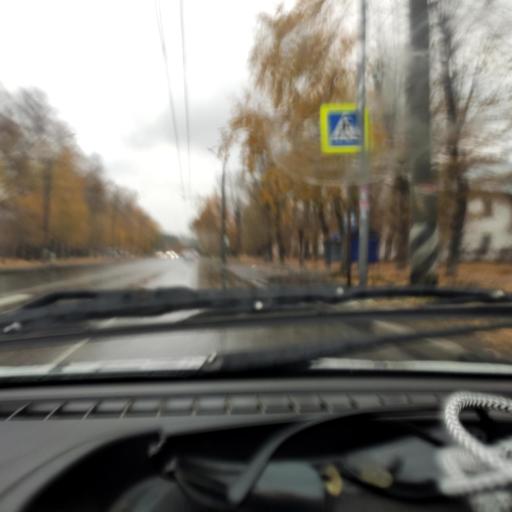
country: RU
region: Samara
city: Tol'yatti
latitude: 53.5027
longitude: 49.3903
